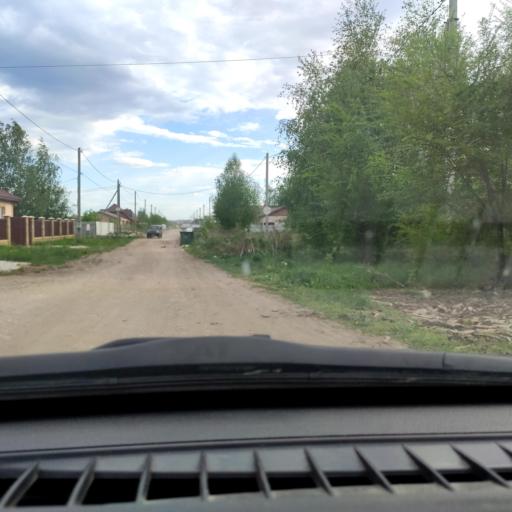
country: RU
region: Samara
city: Tol'yatti
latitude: 53.5723
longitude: 49.4113
